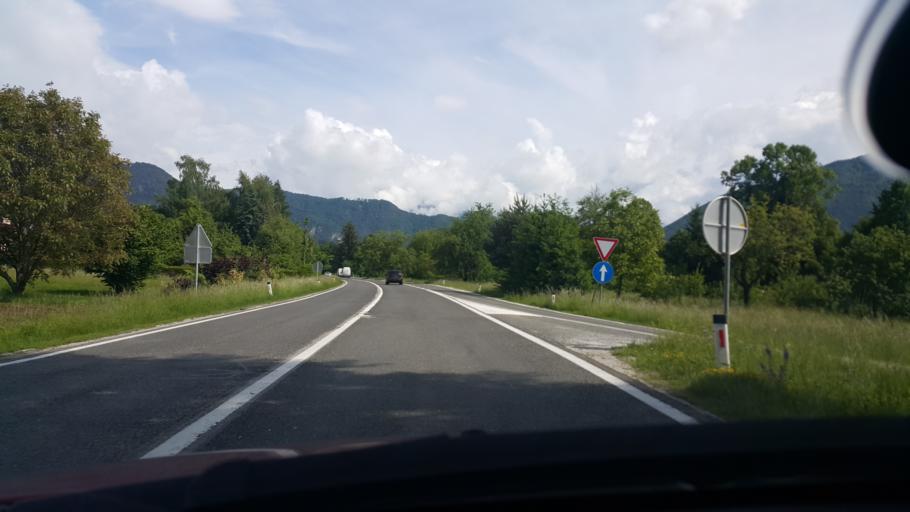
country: SI
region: Trzic
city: Bistrica pri Trzicu
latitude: 46.3276
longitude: 14.2811
